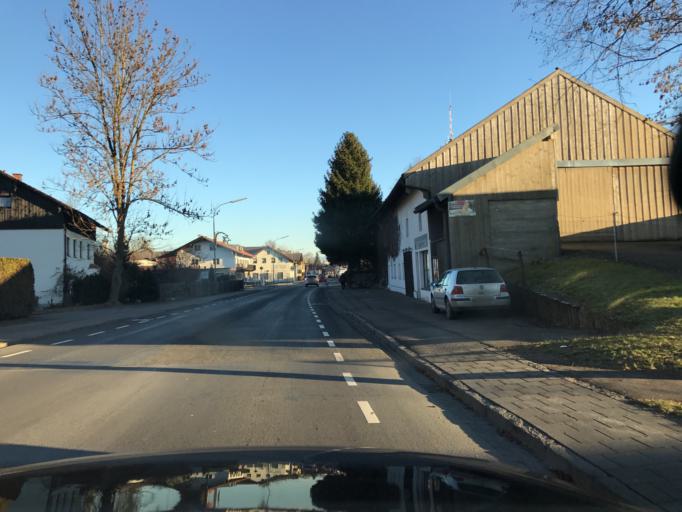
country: DE
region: Bavaria
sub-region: Upper Bavaria
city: Bad Aibling
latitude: 47.8666
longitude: 12.0021
